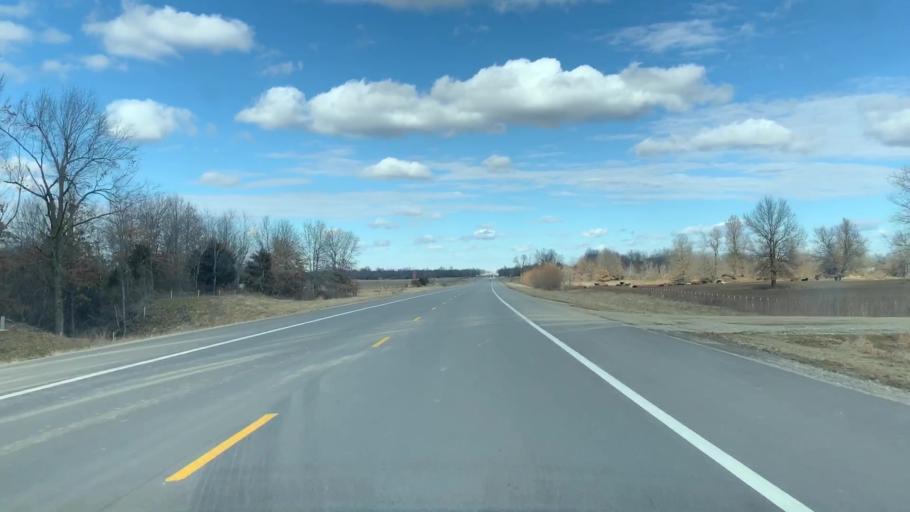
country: US
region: Kansas
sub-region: Cherokee County
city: Columbus
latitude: 37.2615
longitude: -94.8320
